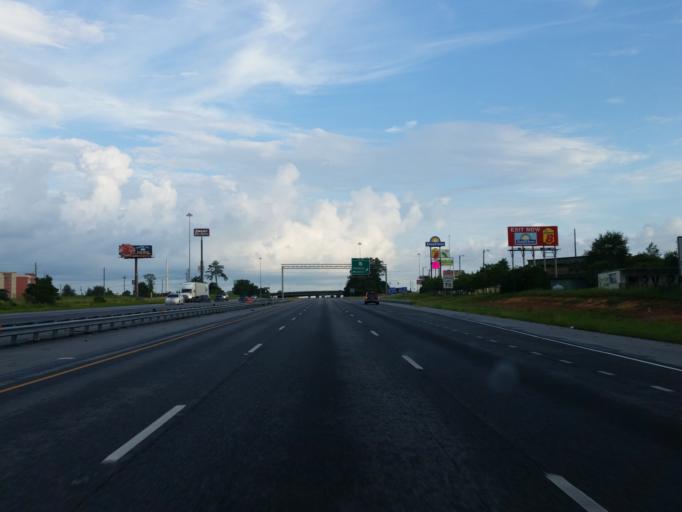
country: US
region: Georgia
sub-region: Lowndes County
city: Remerton
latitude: 30.8499
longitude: -83.3327
